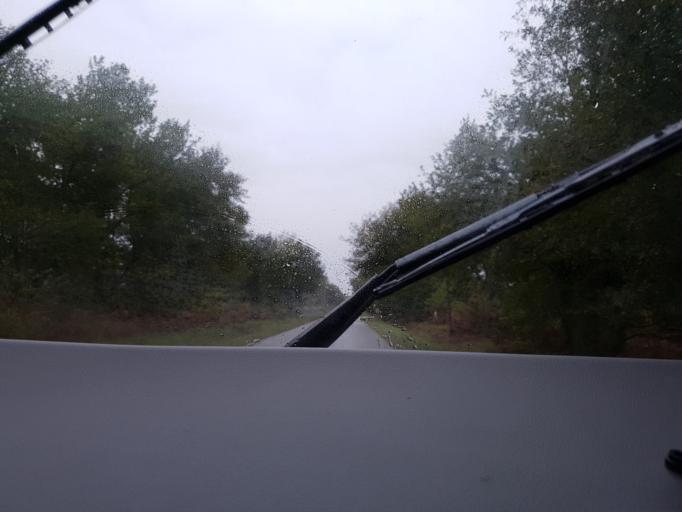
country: FR
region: Aquitaine
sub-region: Departement de la Gironde
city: Saint-Symphorien
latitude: 44.2645
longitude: -0.5326
